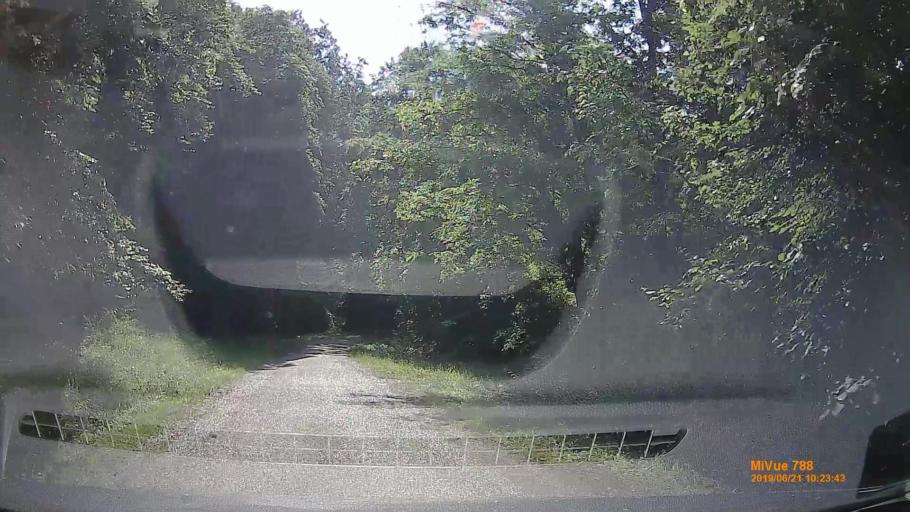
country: HU
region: Baranya
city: Buekkoesd
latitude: 46.1847
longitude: 17.9712
